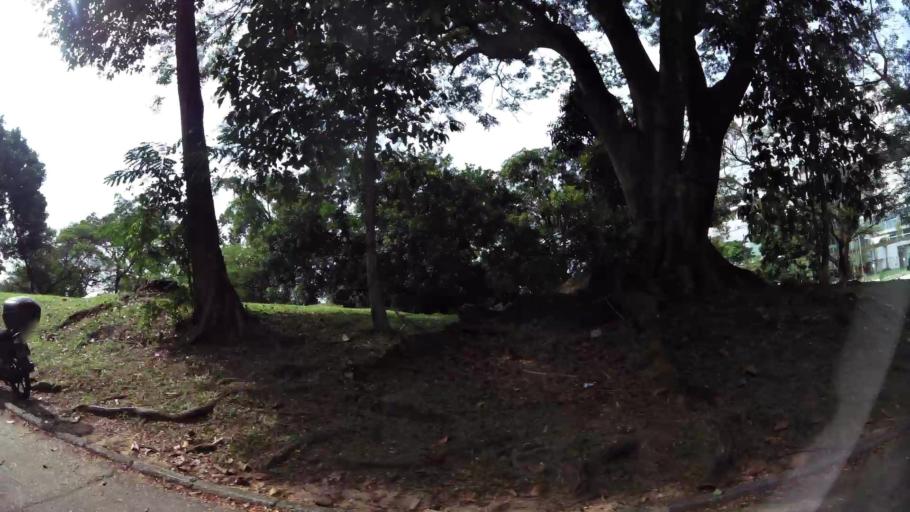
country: SG
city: Singapore
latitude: 1.2961
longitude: 103.7942
